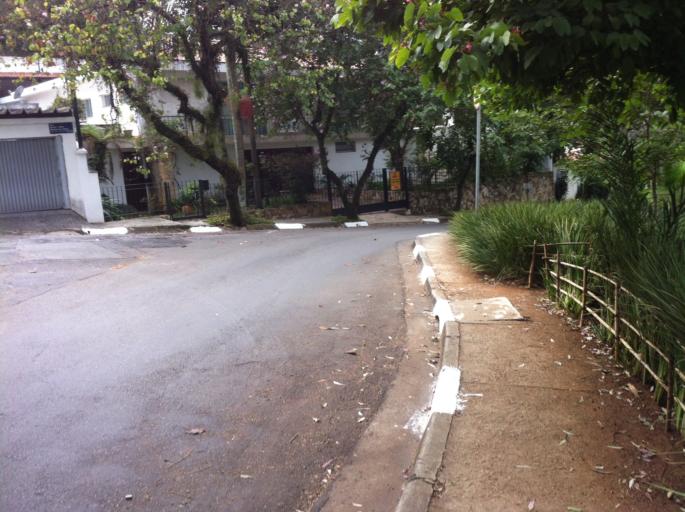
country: BR
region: Sao Paulo
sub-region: Diadema
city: Diadema
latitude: -23.6537
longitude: -46.6838
